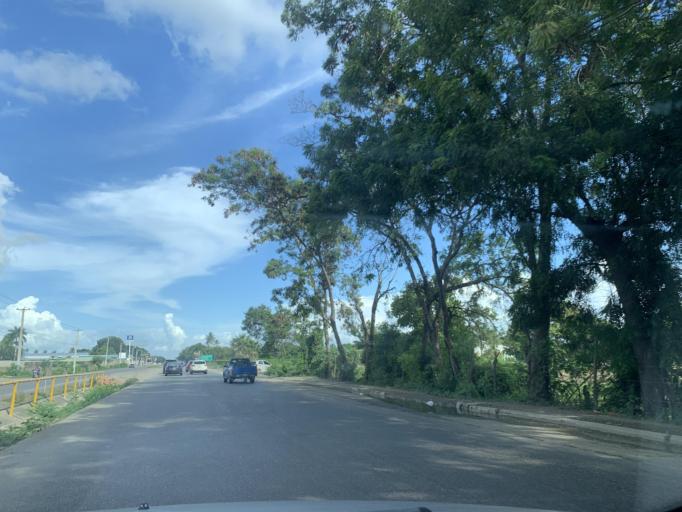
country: DO
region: Santiago
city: Villa Gonzalez
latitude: 19.5447
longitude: -70.8037
